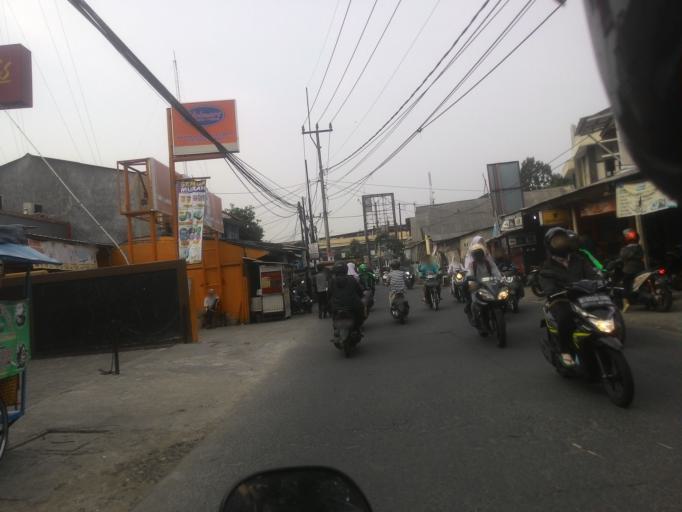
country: ID
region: West Java
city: Depok
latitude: -6.3771
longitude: 106.8137
